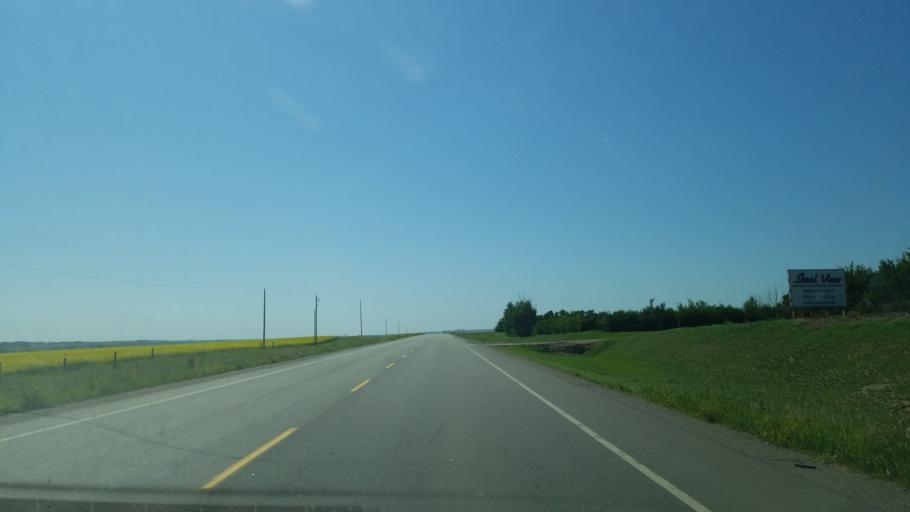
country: CA
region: Saskatchewan
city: Macklin
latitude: 52.3613
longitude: -110.0377
